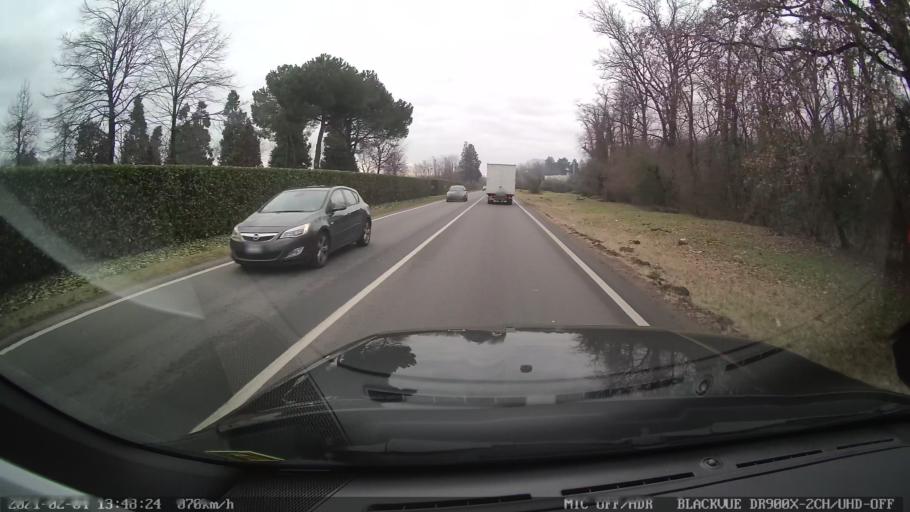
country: IT
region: Lombardy
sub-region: Provincia di Varese
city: Solbiate Olona
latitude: 45.6512
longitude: 8.8672
